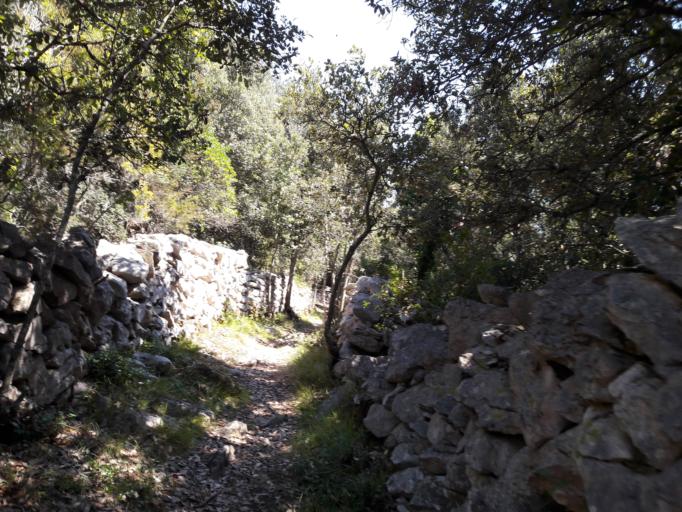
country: HR
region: Licko-Senjska
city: Novalja
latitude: 44.3616
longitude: 14.6979
